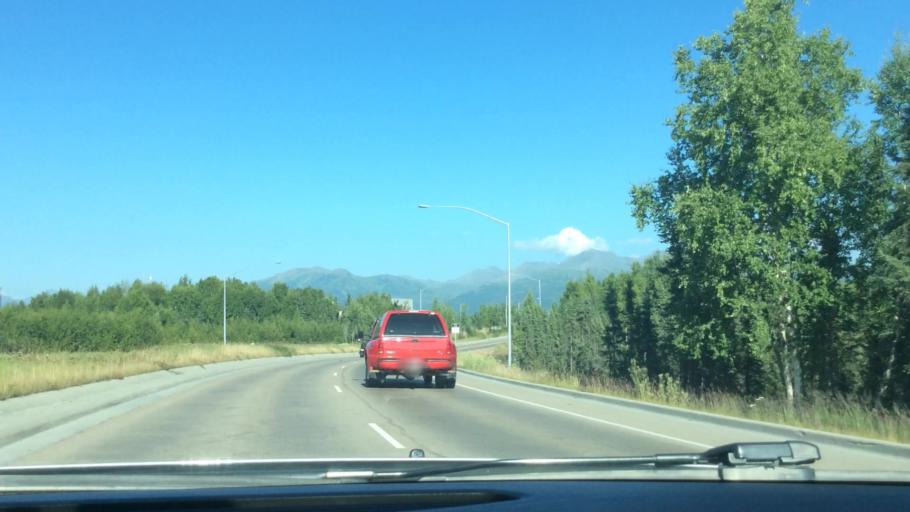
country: US
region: Alaska
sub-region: Anchorage Municipality
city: Anchorage
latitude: 61.1784
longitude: -149.8020
